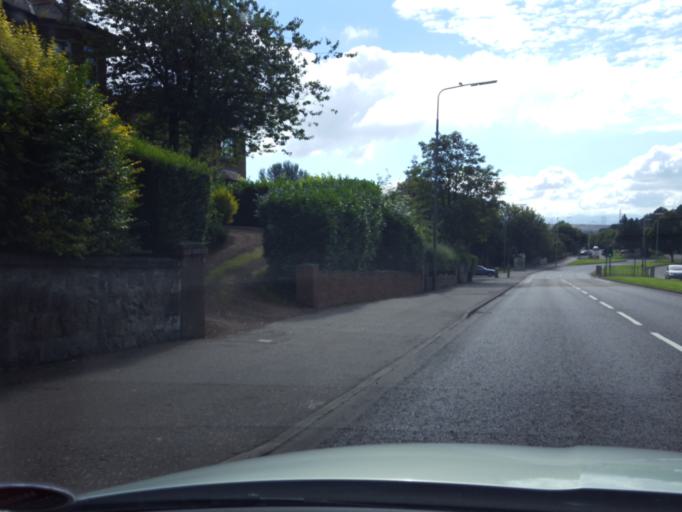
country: GB
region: Scotland
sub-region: Fife
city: Dunfermline
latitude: 56.0600
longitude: -3.4431
